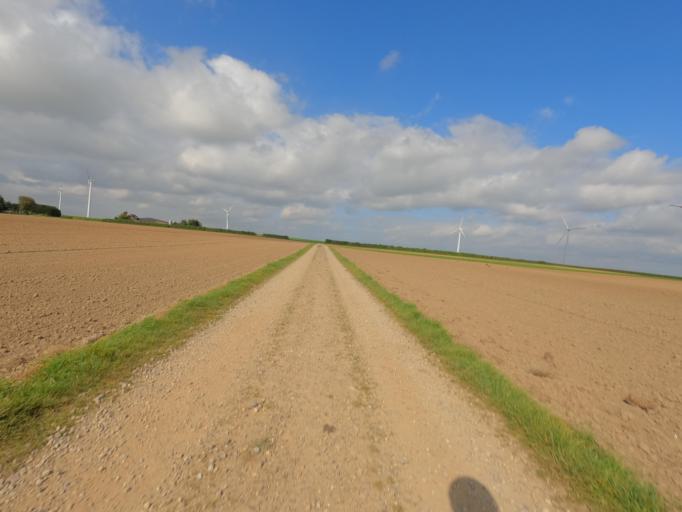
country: DE
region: North Rhine-Westphalia
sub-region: Regierungsbezirk Koln
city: Ubach-Palenberg
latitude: 50.9278
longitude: 6.1454
